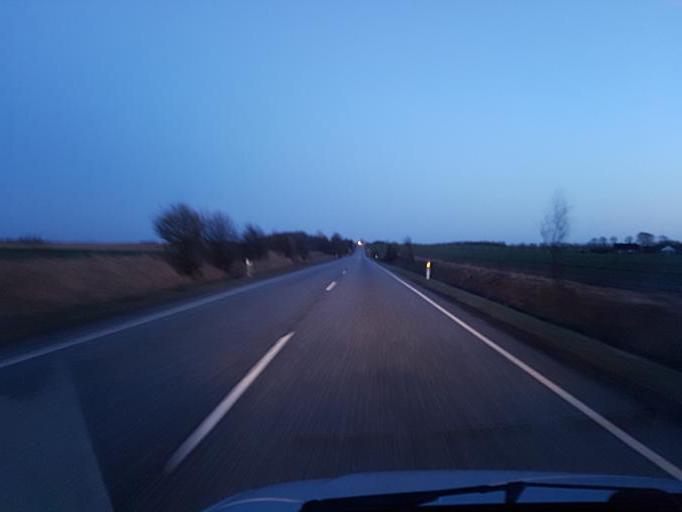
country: DK
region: Central Jutland
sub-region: Ringkobing-Skjern Kommune
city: Skjern
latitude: 56.0415
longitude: 8.5032
